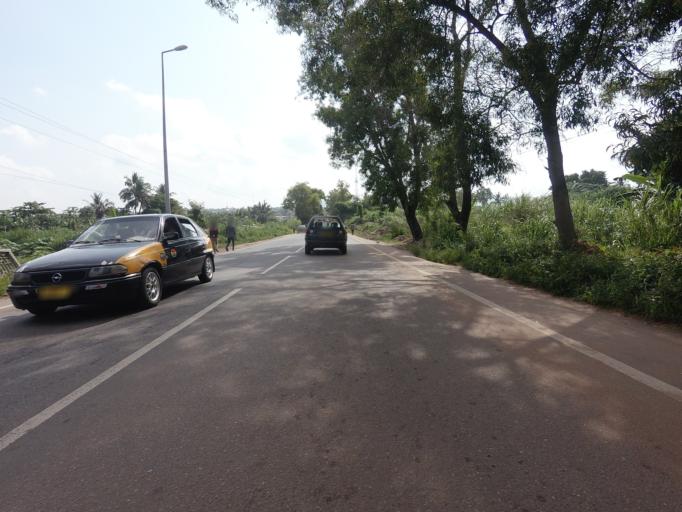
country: GH
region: Volta
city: Ho
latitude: 6.6023
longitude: 0.4914
